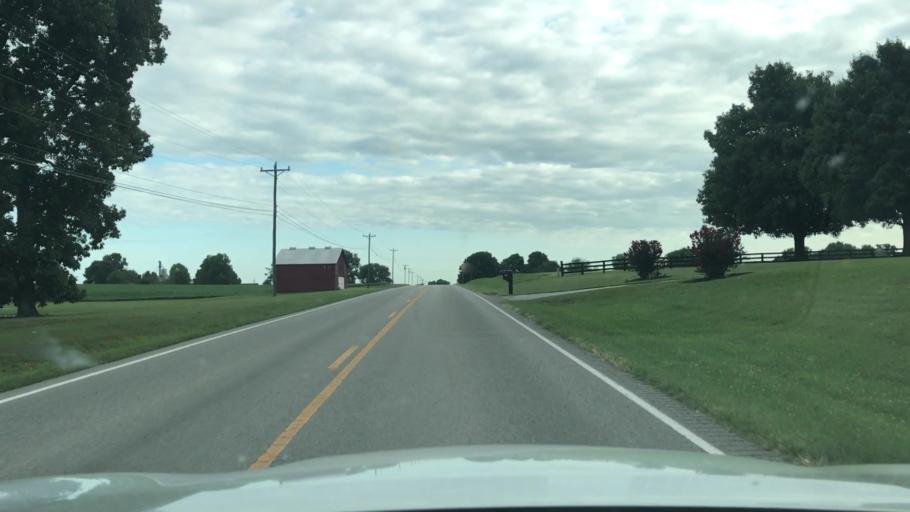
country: US
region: Kentucky
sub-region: Todd County
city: Elkton
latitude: 36.7624
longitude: -87.1672
